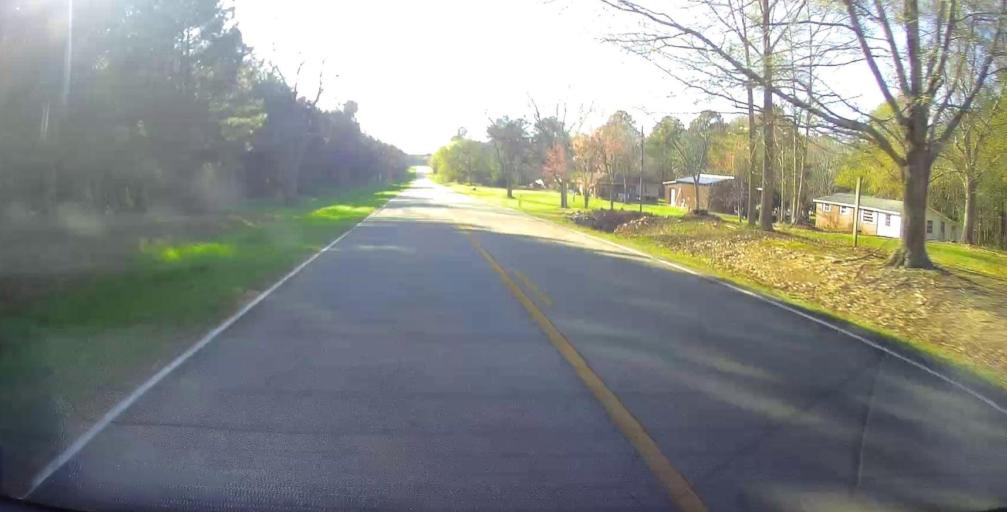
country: US
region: Georgia
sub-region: Houston County
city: Perry
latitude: 32.3739
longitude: -83.7132
